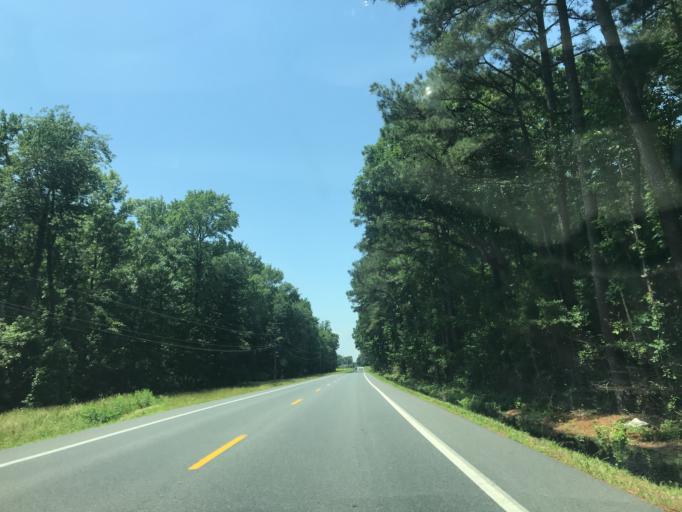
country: US
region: Maryland
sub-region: Dorchester County
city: Hurlock
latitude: 38.6324
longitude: -75.8273
